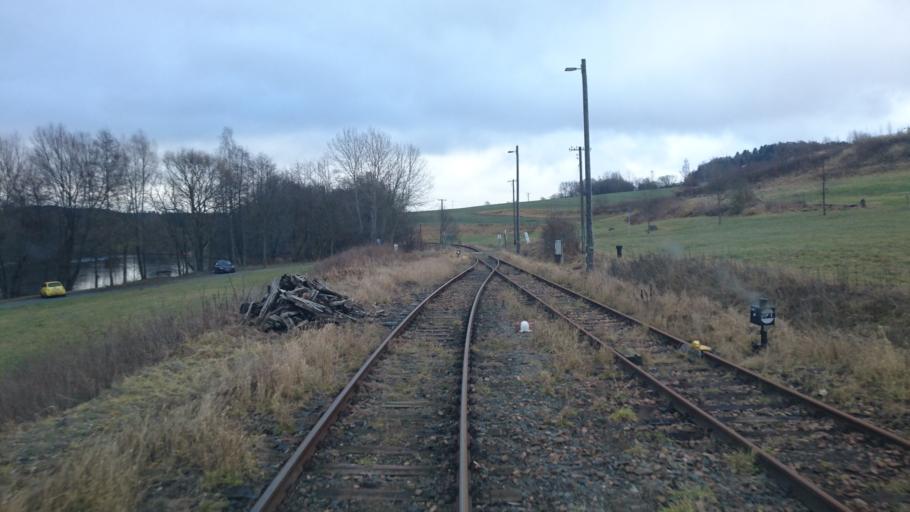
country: DE
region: Thuringia
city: Schleiz
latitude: 50.5821
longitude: 11.8232
